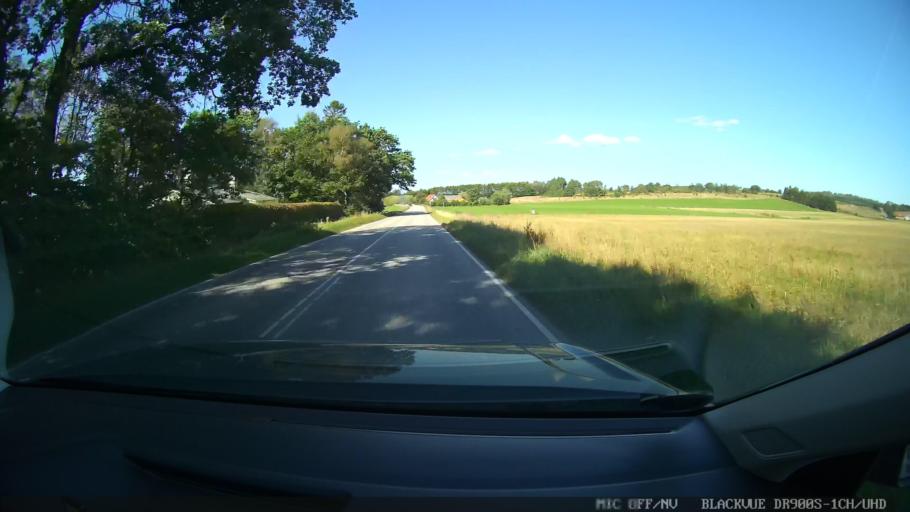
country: DK
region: North Denmark
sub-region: Mariagerfjord Kommune
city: Mariager
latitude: 56.6358
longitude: 9.9772
